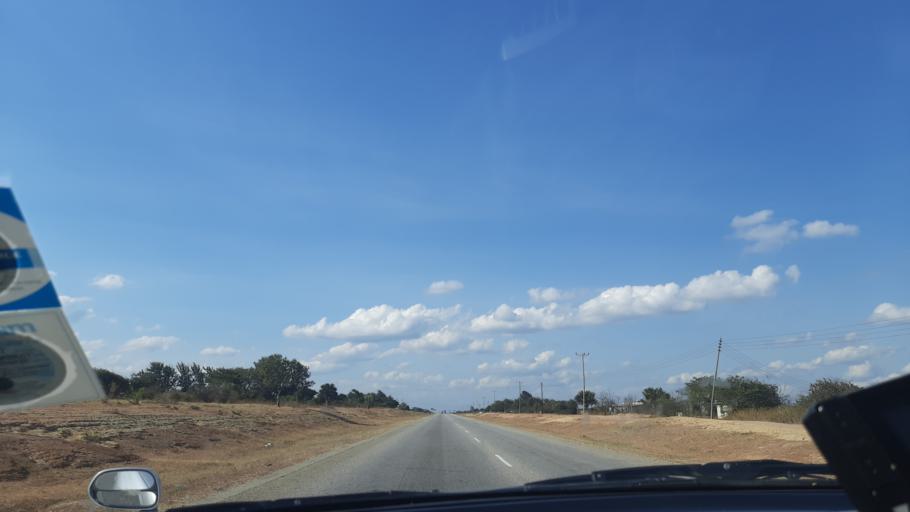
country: TZ
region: Singida
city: Itigi
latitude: -5.5483
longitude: 34.6665
